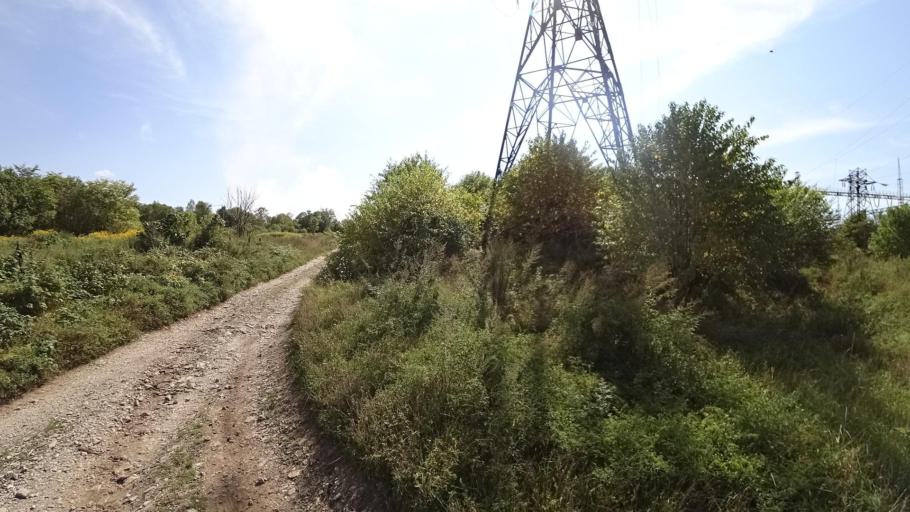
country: RU
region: Jewish Autonomous Oblast
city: Londoko
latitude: 49.0149
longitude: 131.8979
